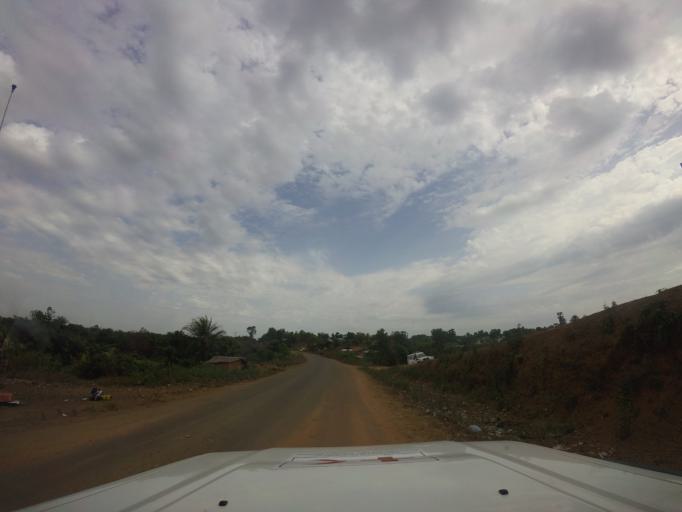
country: LR
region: Grand Cape Mount
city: Robertsport
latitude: 6.8186
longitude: -11.1370
